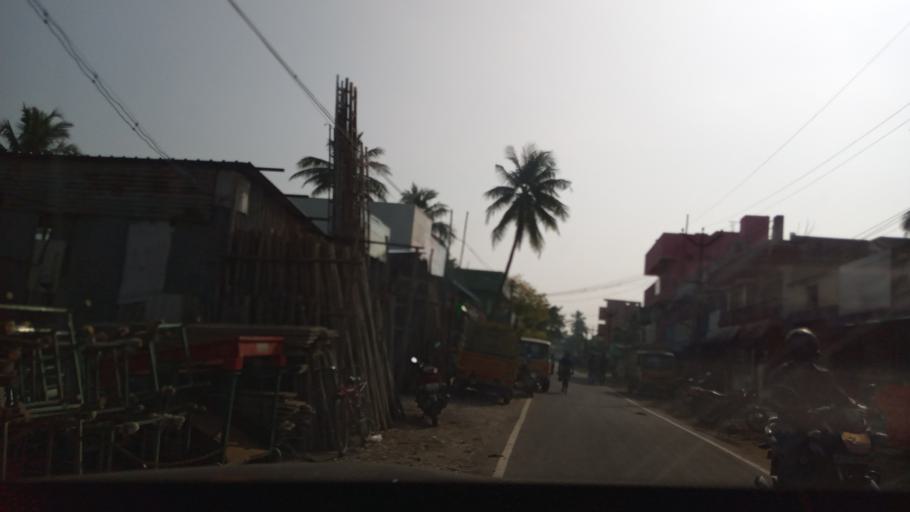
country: IN
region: Tamil Nadu
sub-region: Kancheepuram
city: Guduvancheri
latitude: 12.8521
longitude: 80.0679
